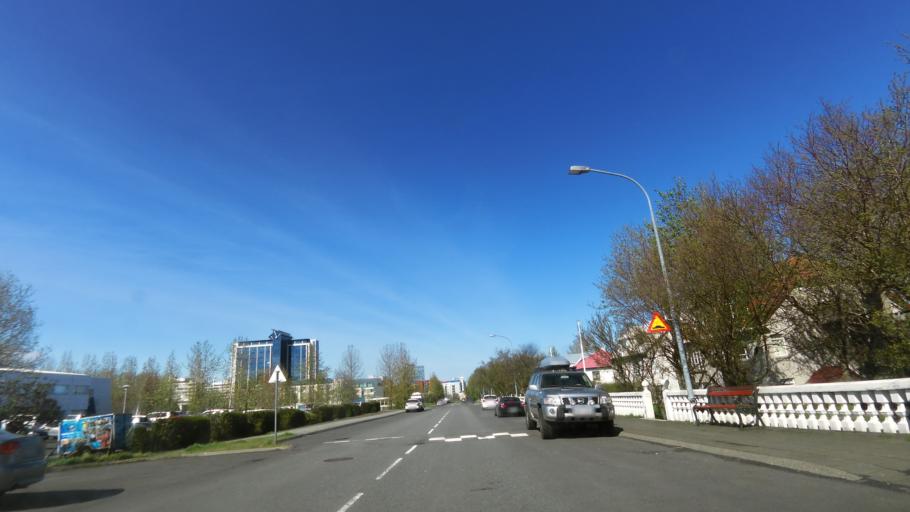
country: IS
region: Capital Region
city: Reykjavik
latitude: 64.1420
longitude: -21.8854
